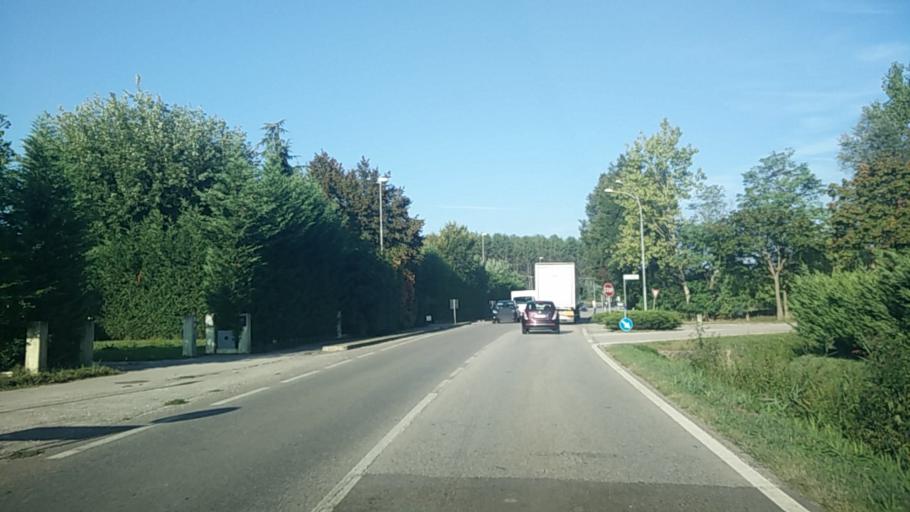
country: IT
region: Veneto
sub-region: Provincia di Venezia
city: Moniego
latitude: 45.5767
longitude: 12.0911
